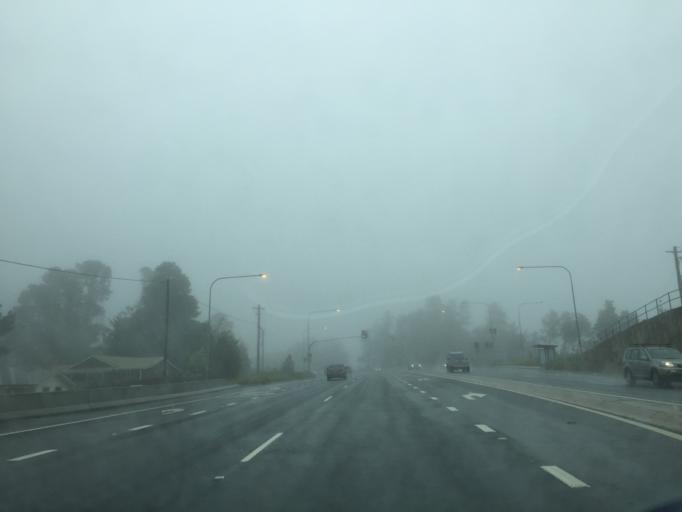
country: AU
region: New South Wales
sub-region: Blue Mountains Municipality
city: Lawson
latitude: -33.7182
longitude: 150.3828
